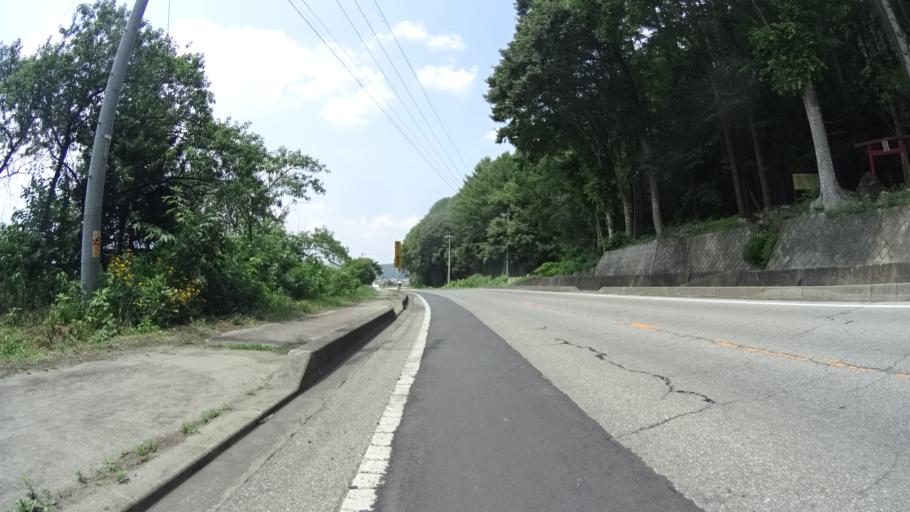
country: JP
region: Nagano
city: Saku
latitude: 36.1472
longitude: 138.5148
